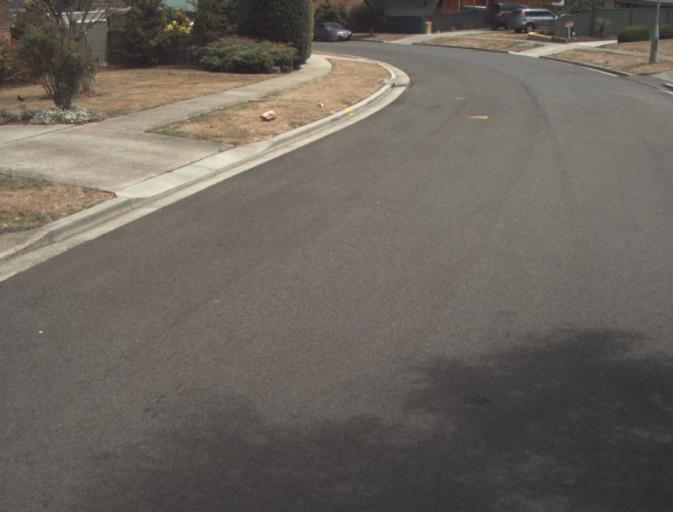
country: AU
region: Tasmania
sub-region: Launceston
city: Mayfield
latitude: -41.3789
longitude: 147.1184
